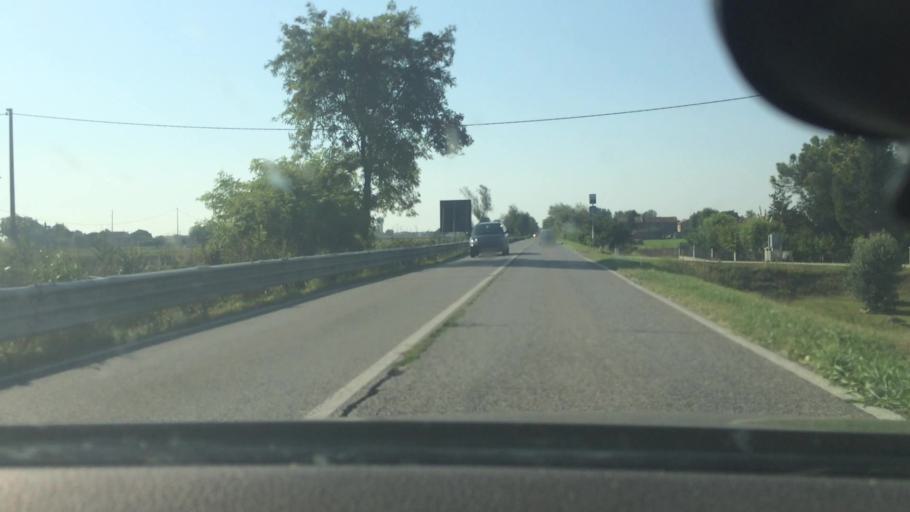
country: IT
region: Emilia-Romagna
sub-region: Provincia di Ferrara
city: Comacchio
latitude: 44.7119
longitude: 12.1602
